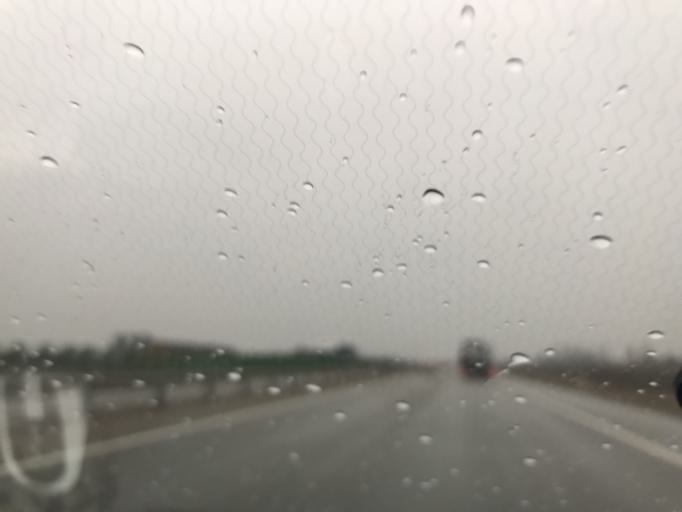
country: RU
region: Krasnodarskiy
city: Krylovskaya
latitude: 46.2925
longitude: 39.8219
